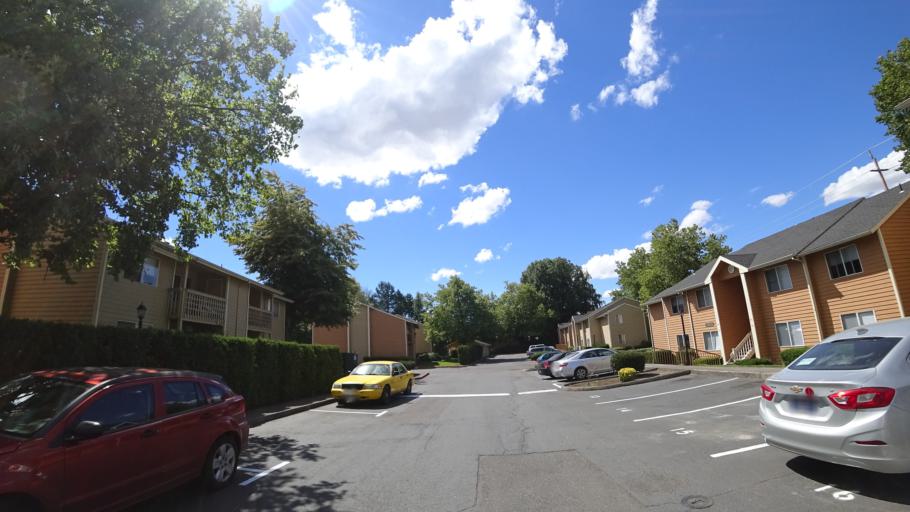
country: US
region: Oregon
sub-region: Multnomah County
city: Fairview
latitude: 45.5496
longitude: -122.4988
